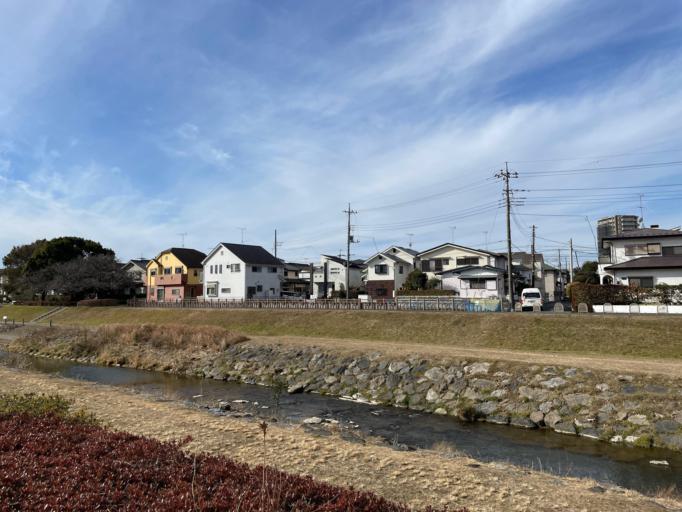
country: JP
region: Saitama
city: Tokorozawa
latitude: 35.7879
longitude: 139.5141
